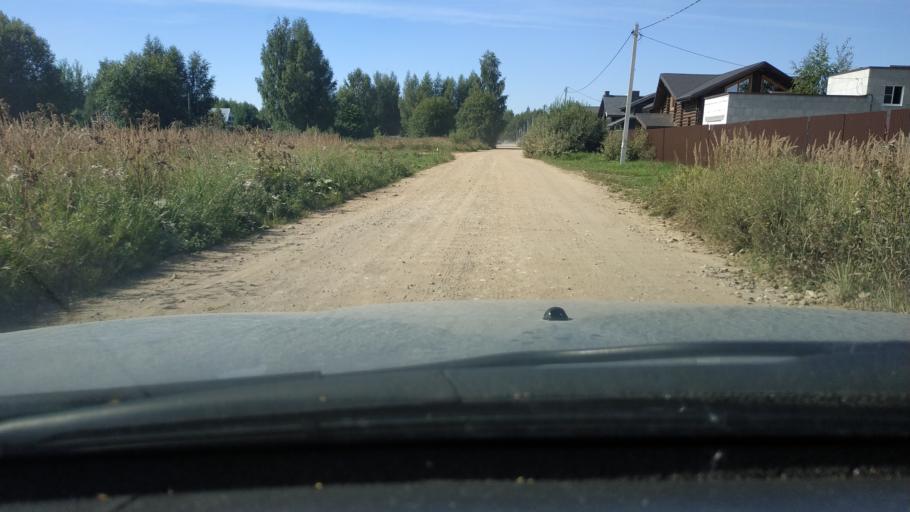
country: RU
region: Kostroma
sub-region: Kostromskoy Rayon
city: Kostroma
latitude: 57.7757
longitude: 40.7371
